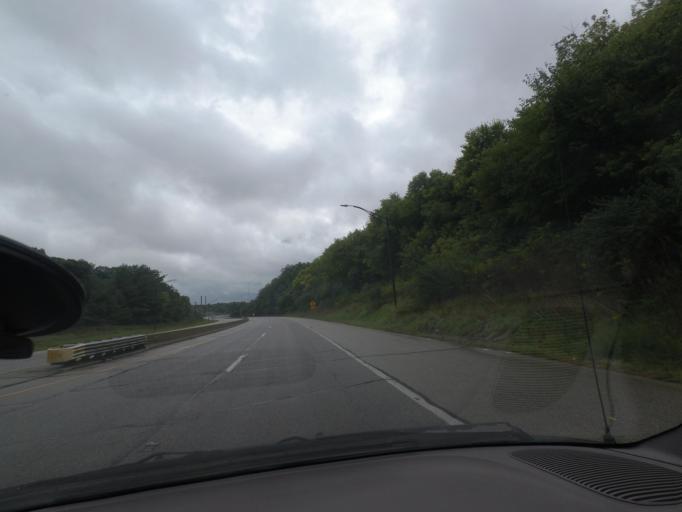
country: US
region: Indiana
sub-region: Montgomery County
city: Crawfordsville
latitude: 40.0560
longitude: -86.9077
